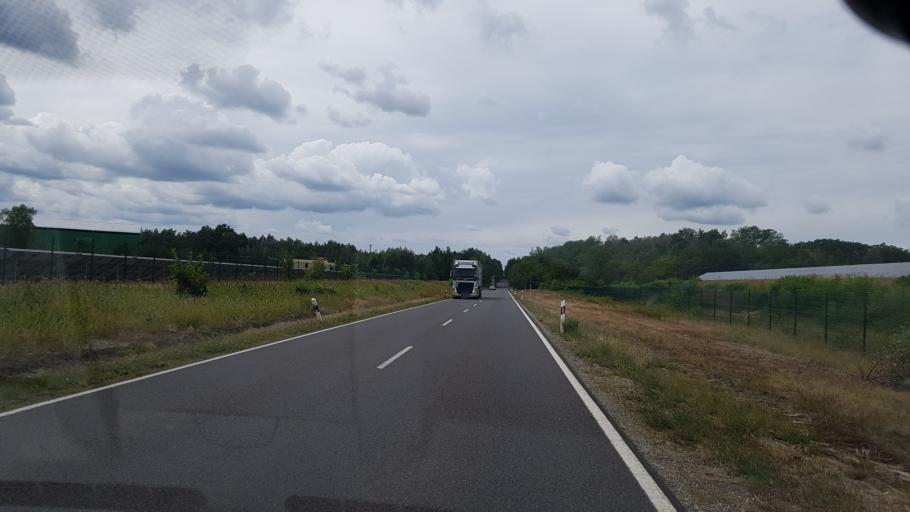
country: DE
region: Brandenburg
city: Spremberg
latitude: 51.5150
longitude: 14.3917
